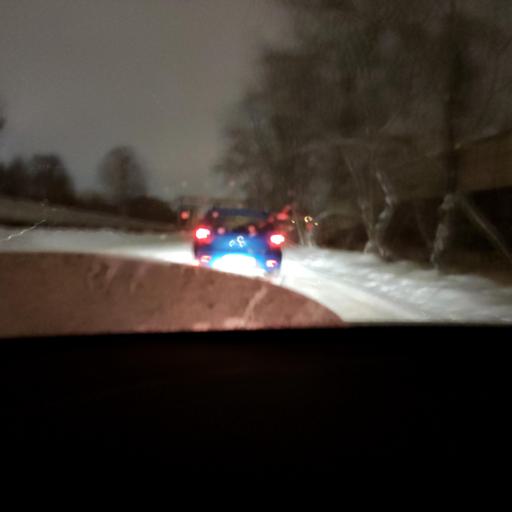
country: RU
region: Tatarstan
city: Staroye Arakchino
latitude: 55.8609
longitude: 48.9835
